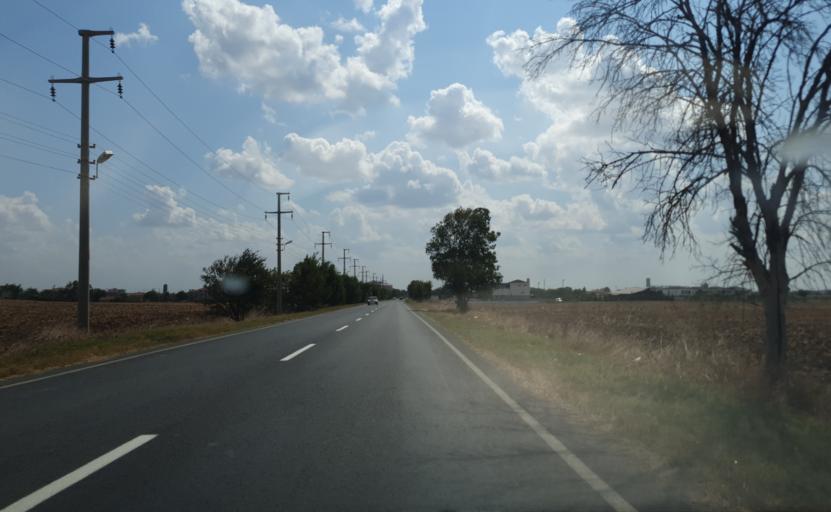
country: TR
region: Kirklareli
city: Luleburgaz
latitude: 41.3678
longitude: 27.3391
